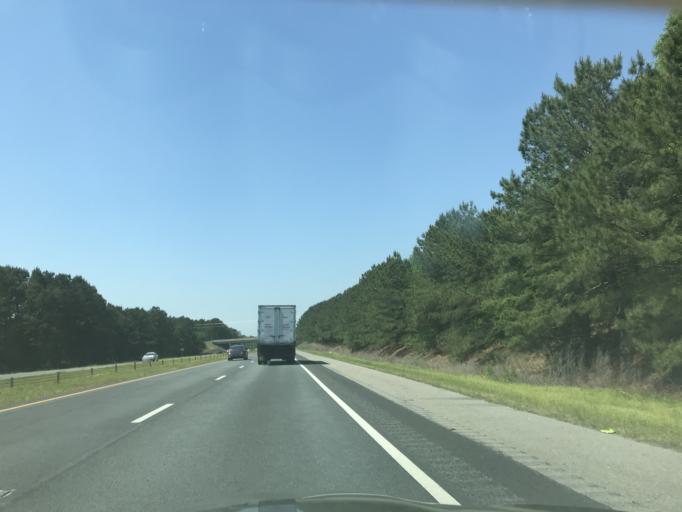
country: US
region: North Carolina
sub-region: Johnston County
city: Benson
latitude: 35.3734
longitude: -78.5018
